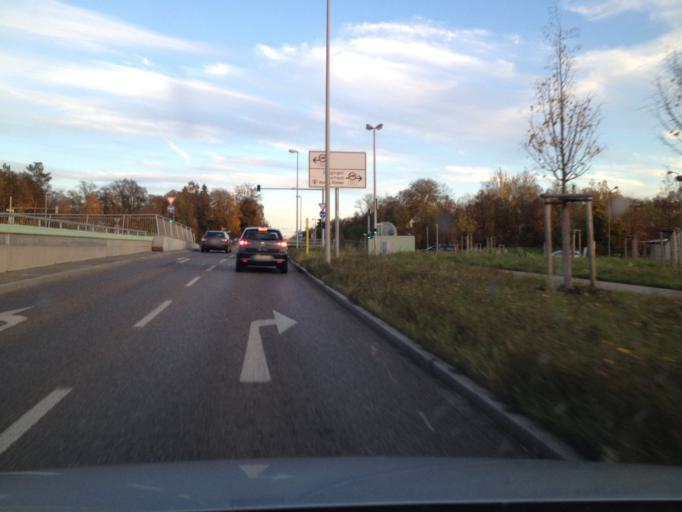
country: DE
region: Bavaria
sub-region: Swabia
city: Stadtbergen
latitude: 48.3480
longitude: 10.8708
